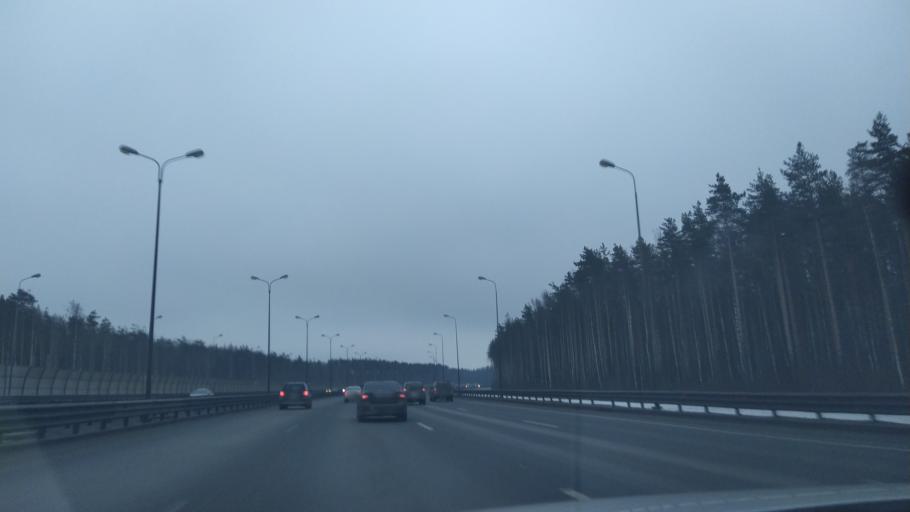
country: RU
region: St.-Petersburg
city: Krasnogvargeisky
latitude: 59.9738
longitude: 30.5422
